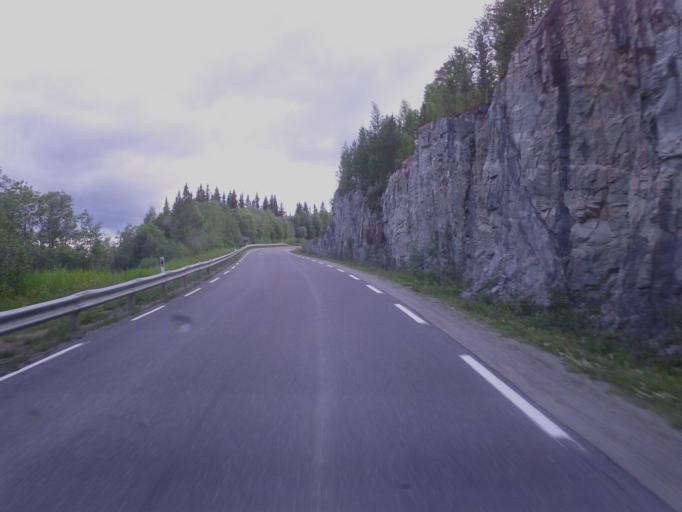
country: NO
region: Nordland
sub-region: Hattfjelldal
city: Hattfjelldal
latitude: 65.6028
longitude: 13.9455
